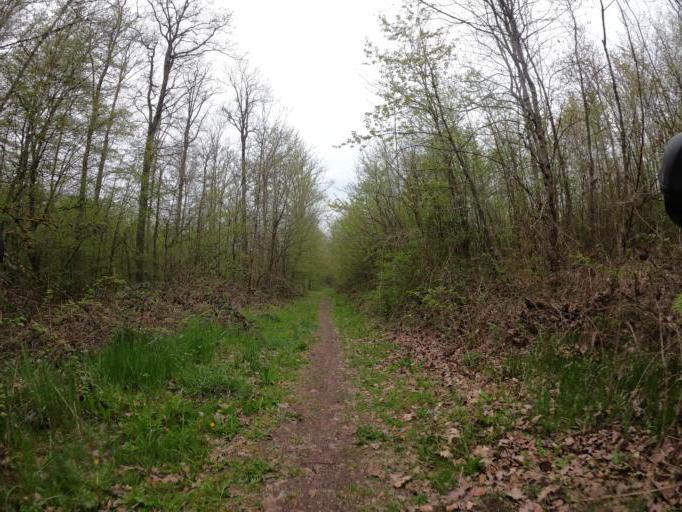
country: DE
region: Baden-Wuerttemberg
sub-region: Karlsruhe Region
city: Illingen
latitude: 48.9663
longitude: 8.9174
